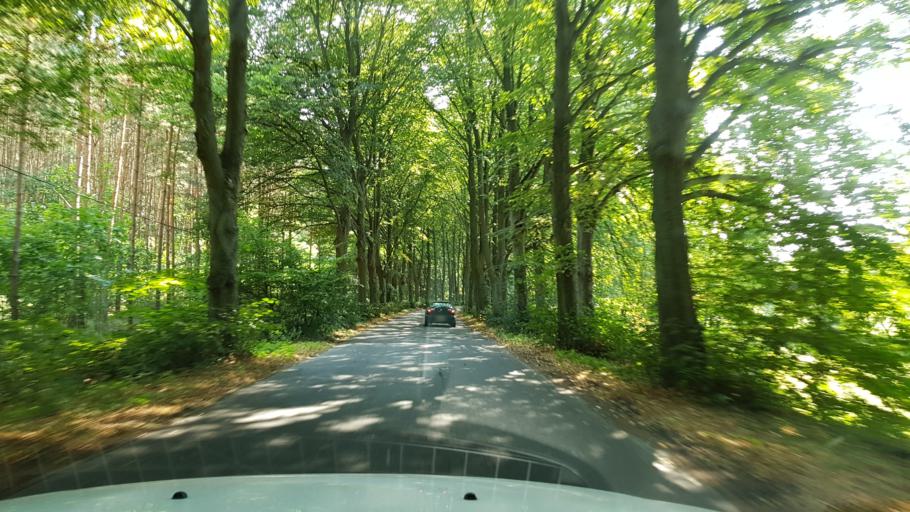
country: PL
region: West Pomeranian Voivodeship
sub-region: Powiat gryfinski
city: Chojna
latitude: 52.9603
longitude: 14.4789
